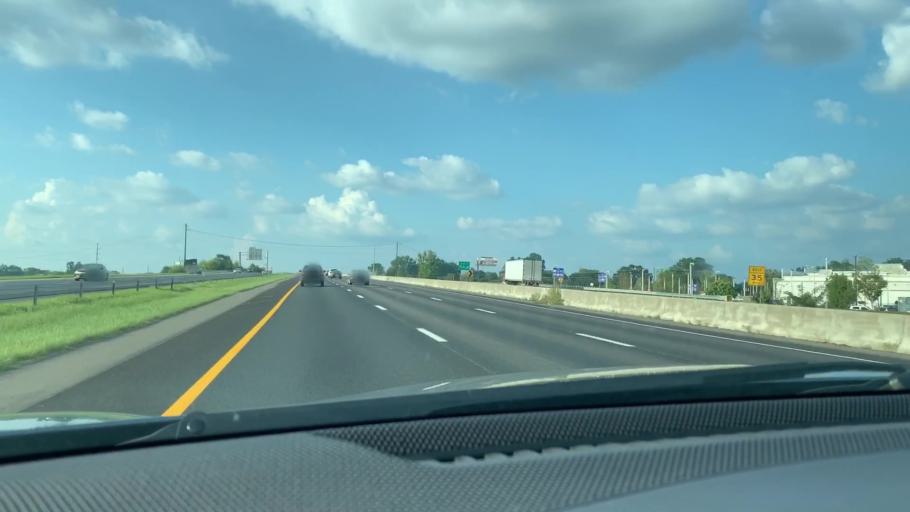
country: US
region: South Carolina
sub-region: Richland County
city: Forest Acres
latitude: 33.9697
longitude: -80.9540
